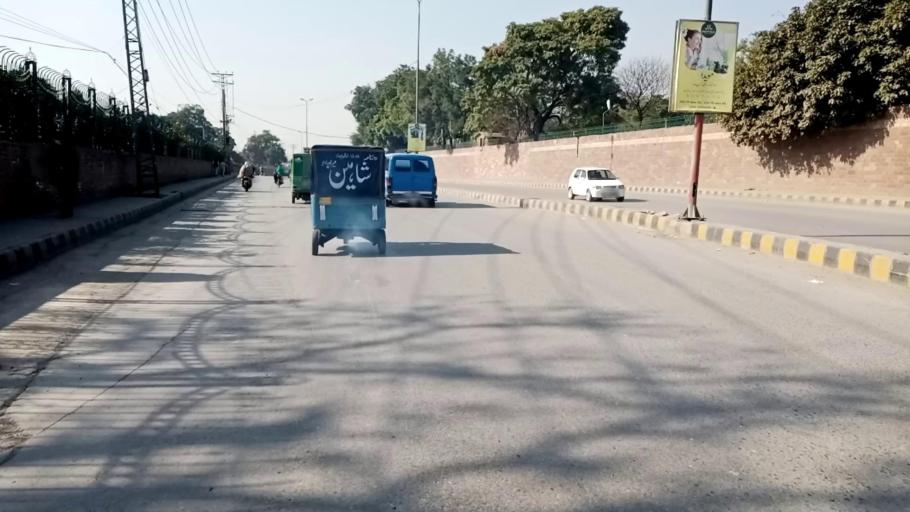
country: PK
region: Khyber Pakhtunkhwa
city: Peshawar
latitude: 34.0085
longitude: 71.5583
